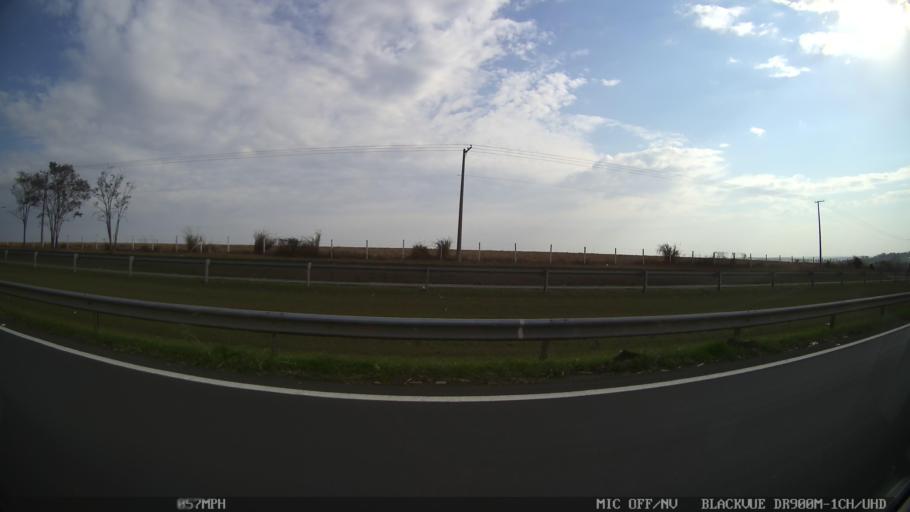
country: BR
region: Sao Paulo
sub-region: Paulinia
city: Paulinia
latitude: -22.7043
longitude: -47.1446
